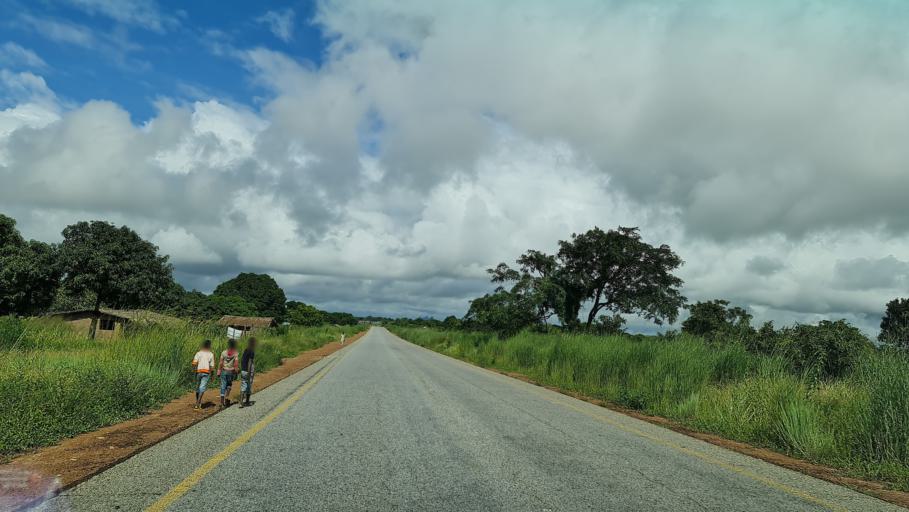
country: MZ
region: Nampula
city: Nampula
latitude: -15.0249
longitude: 38.4692
